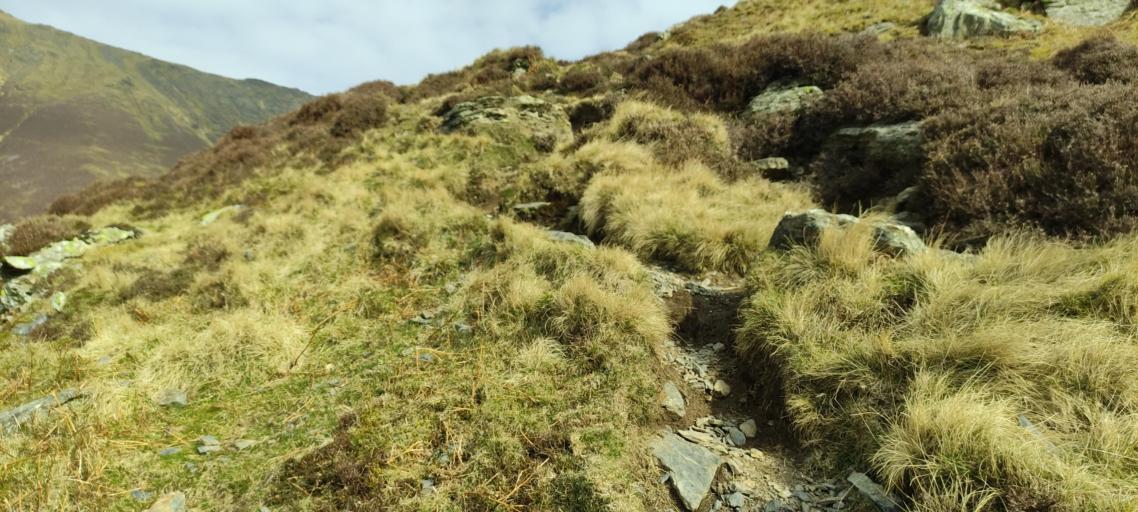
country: GB
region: England
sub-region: Cumbria
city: Keswick
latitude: 54.6290
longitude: -3.0465
